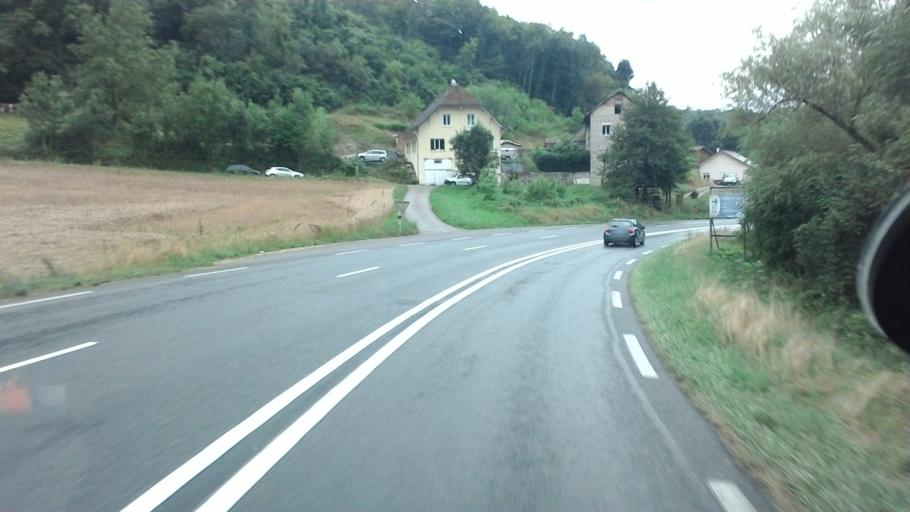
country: FR
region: Rhone-Alpes
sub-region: Departement de la Savoie
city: Le Bourget-du-Lac
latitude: 45.6895
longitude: 5.8252
